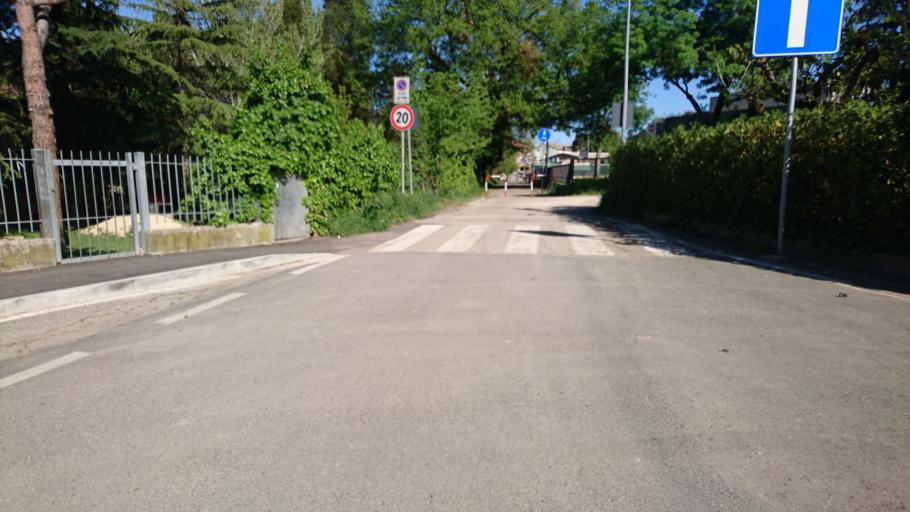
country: IT
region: The Marches
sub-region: Provincia di Pesaro e Urbino
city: Pesaro
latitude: 43.8991
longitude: 12.8939
